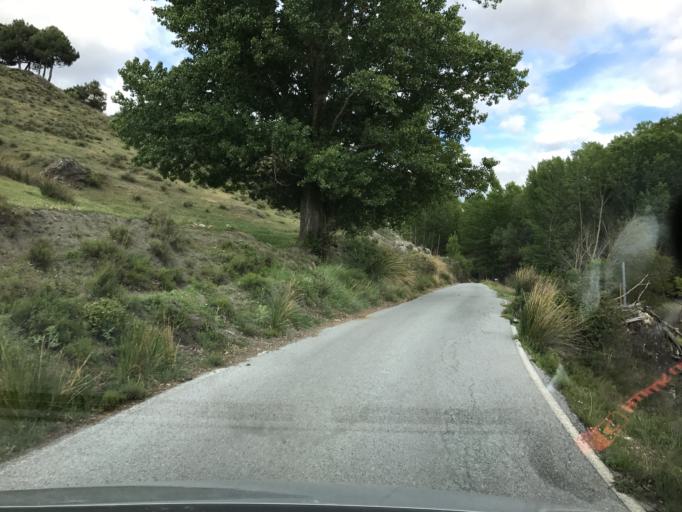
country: ES
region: Andalusia
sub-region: Provincia de Granada
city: Diezma
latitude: 37.2418
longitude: -3.3762
